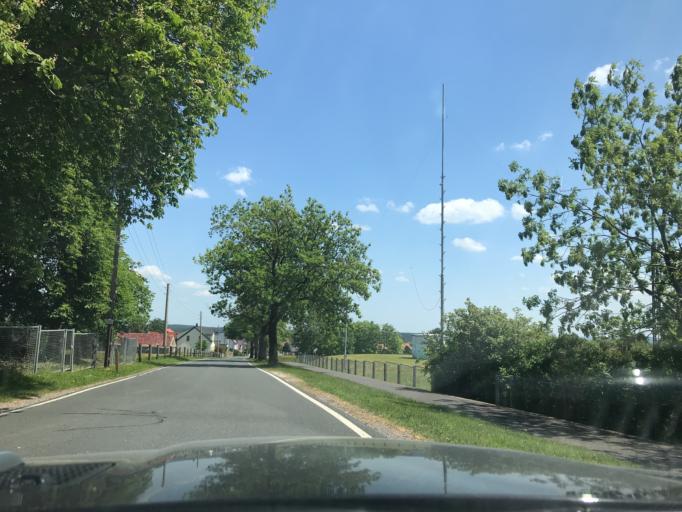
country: DE
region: Thuringia
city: Ilmenau
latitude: 50.7011
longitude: 10.9204
